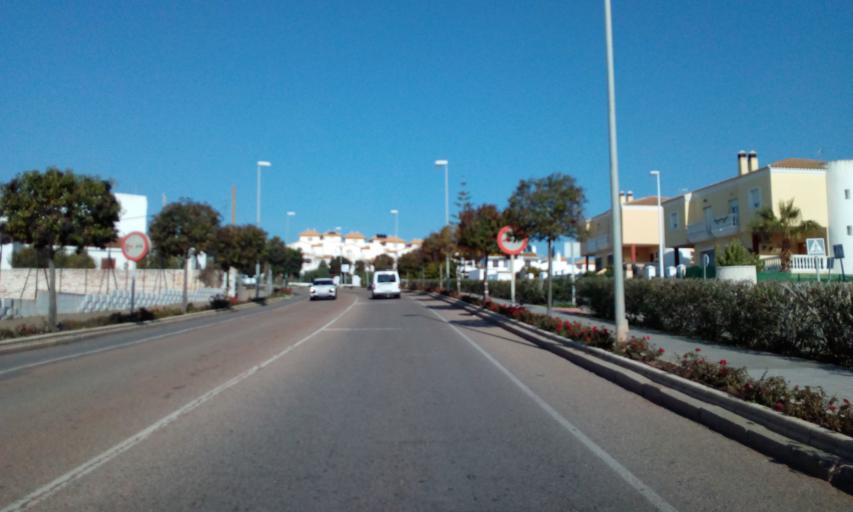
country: ES
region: Andalusia
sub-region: Provincia de Huelva
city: Ayamonte
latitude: 37.2179
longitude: -7.3947
